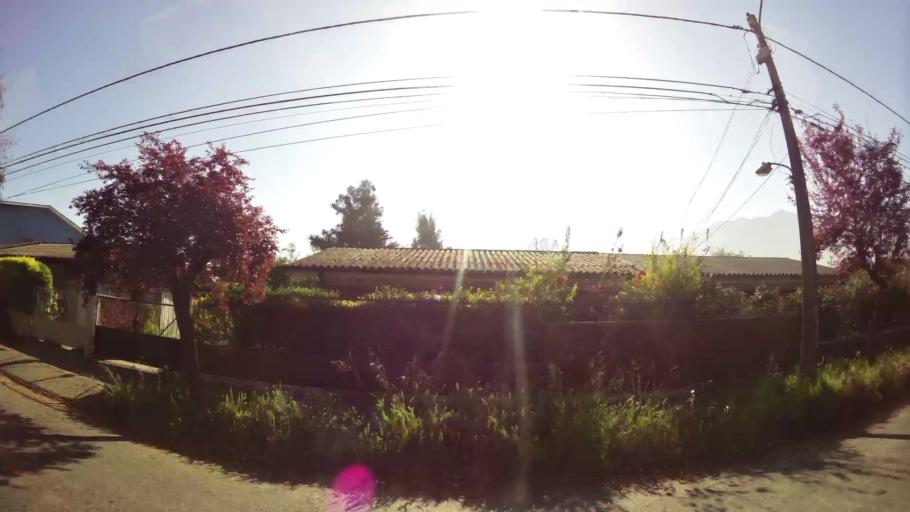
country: CL
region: Santiago Metropolitan
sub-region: Provincia de Santiago
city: Villa Presidente Frei, Nunoa, Santiago, Chile
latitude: -33.4599
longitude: -70.5529
